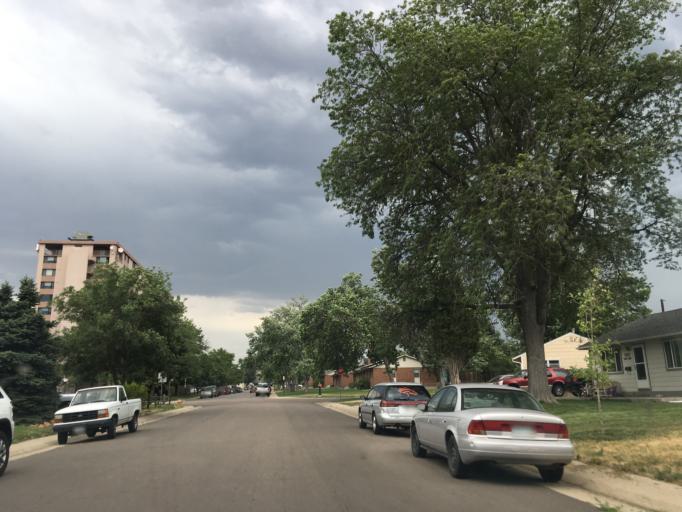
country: US
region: Colorado
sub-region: Arapahoe County
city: Sheridan
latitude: 39.6683
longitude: -105.0261
